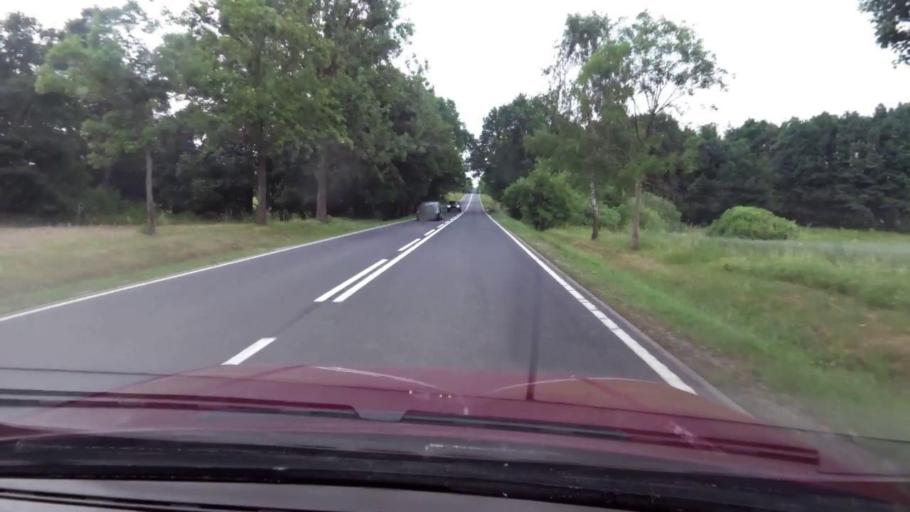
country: PL
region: Pomeranian Voivodeship
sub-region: Powiat bytowski
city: Trzebielino
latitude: 54.2657
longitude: 17.1001
